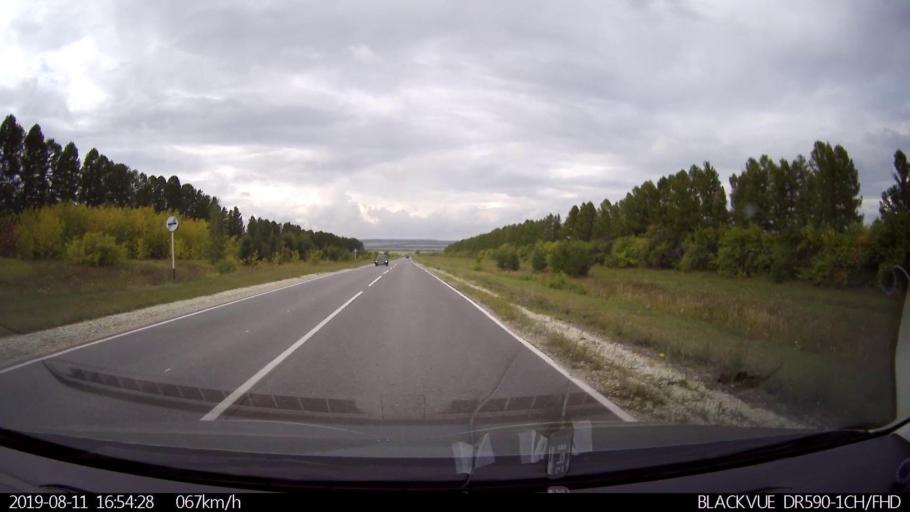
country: RU
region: Ulyanovsk
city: Mayna
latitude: 54.2730
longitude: 47.6663
